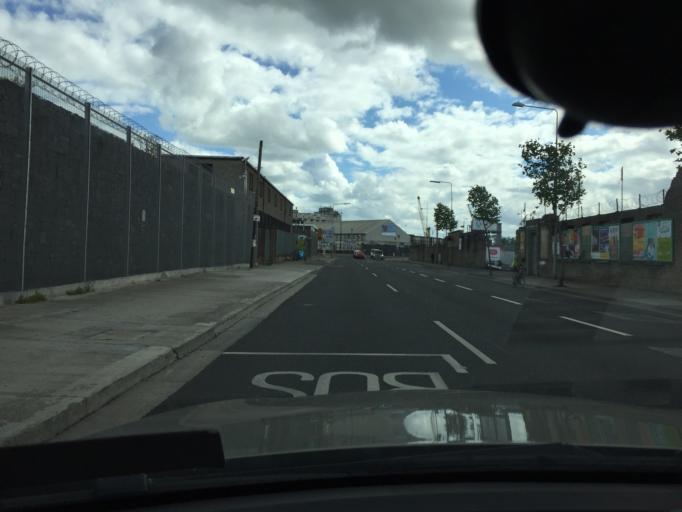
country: IE
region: Leinster
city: Ringsend
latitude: 53.3535
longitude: -6.2266
